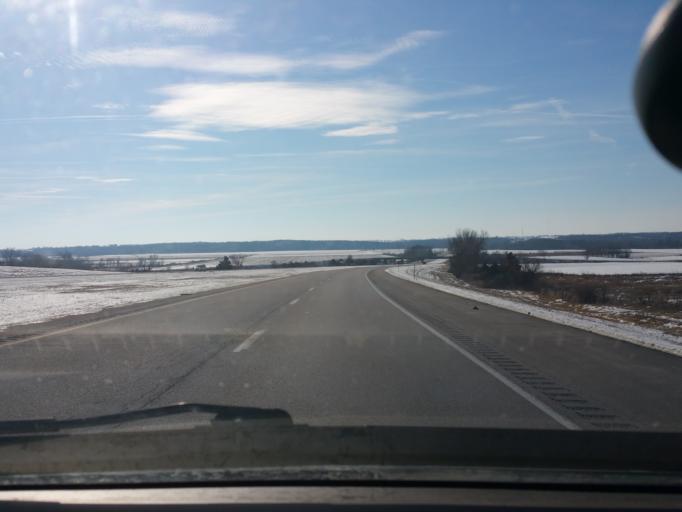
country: US
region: Iowa
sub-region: Decatur County
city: Lamoni
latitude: 40.6884
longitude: -93.8463
